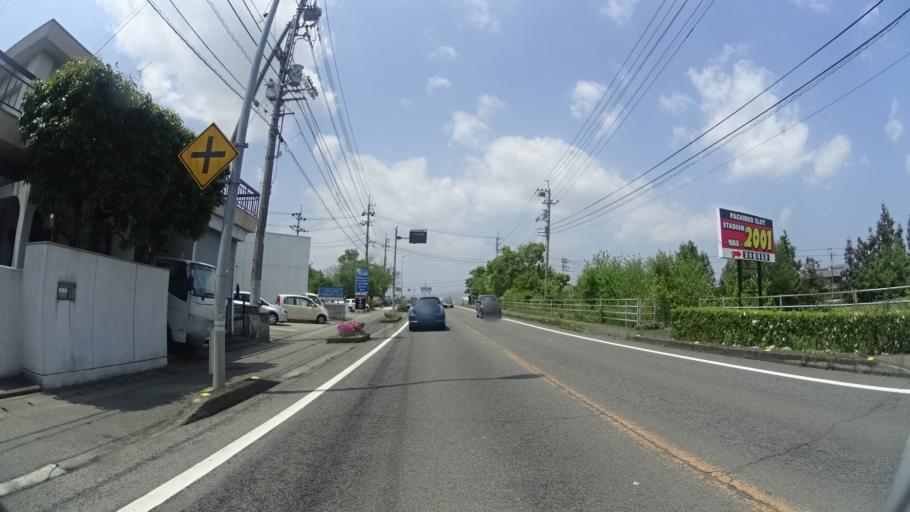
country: JP
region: Tokushima
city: Kamojimacho-jogejima
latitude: 34.0733
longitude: 134.3936
